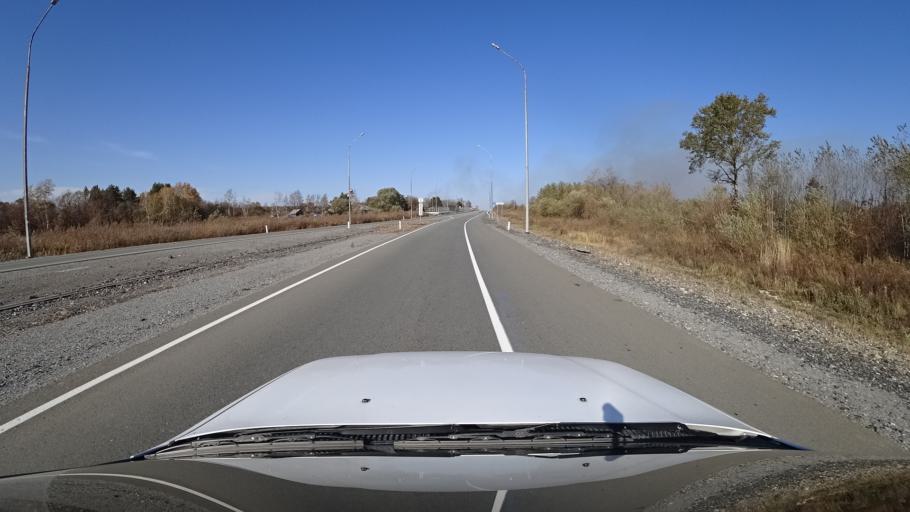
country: RU
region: Primorskiy
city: Dal'nerechensk
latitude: 45.8746
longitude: 133.7255
